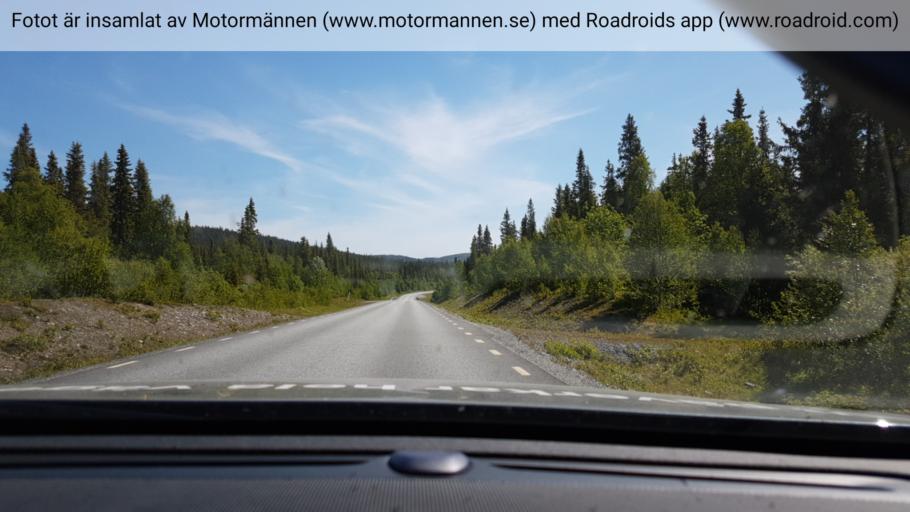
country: SE
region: Vaesterbotten
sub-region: Vilhelmina Kommun
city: Sjoberg
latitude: 64.8114
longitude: 15.2567
